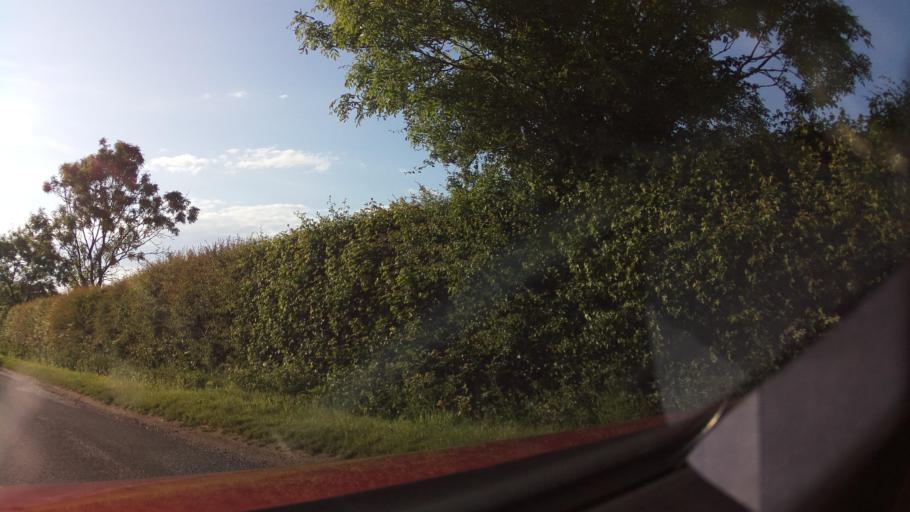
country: GB
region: England
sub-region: Lincolnshire
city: Navenby
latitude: 53.1157
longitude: -0.6203
